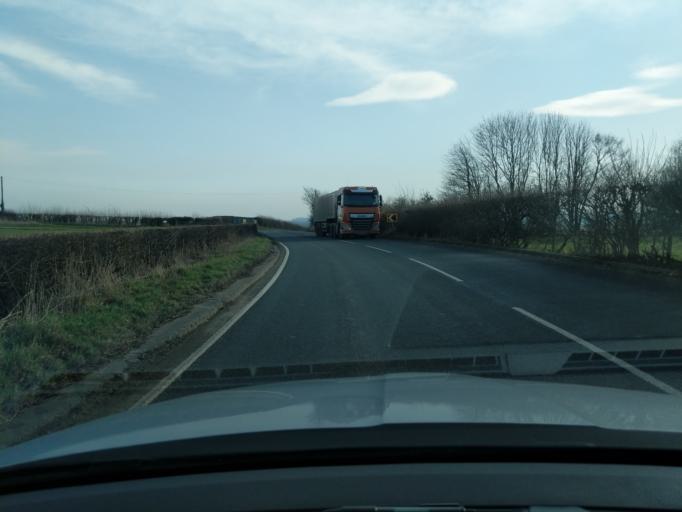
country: GB
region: England
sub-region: North Yorkshire
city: Catterick
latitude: 54.3185
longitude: -1.6768
